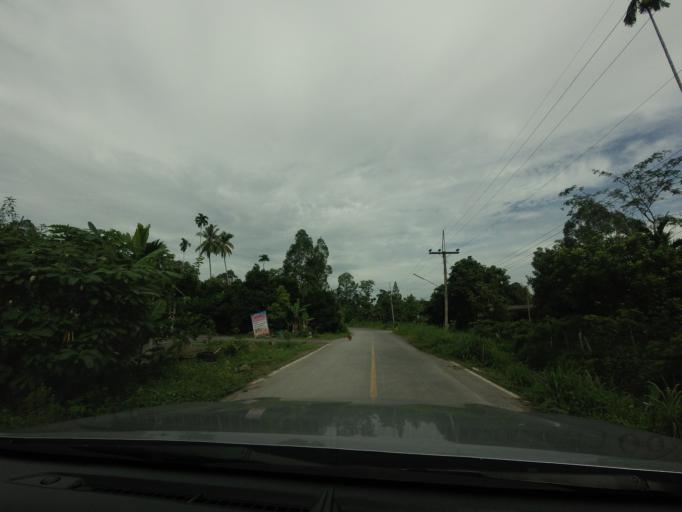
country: TH
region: Nakhon Si Thammarat
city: Phra Phrom
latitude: 8.2853
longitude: 99.9187
